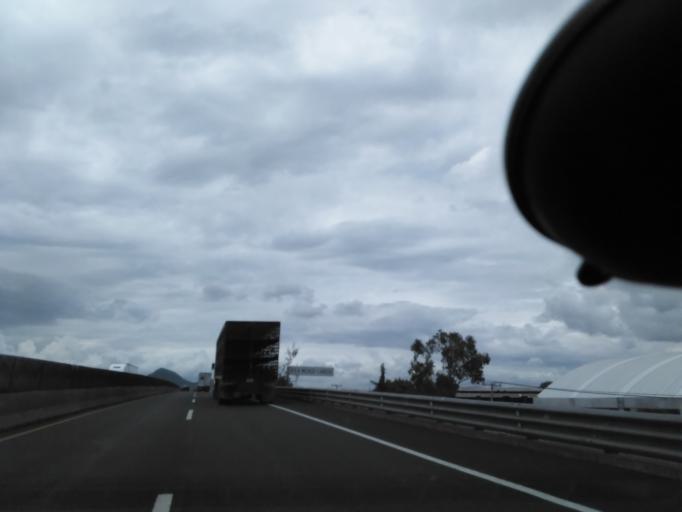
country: MX
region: Morelos
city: San Pedro Xalpa
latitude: 19.8111
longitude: -99.1924
